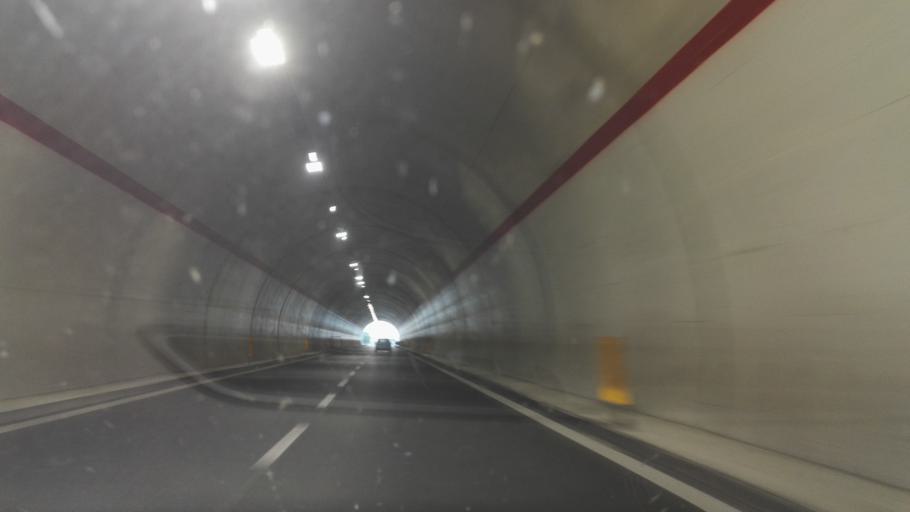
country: IT
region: Calabria
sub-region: Provincia di Reggio Calabria
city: Roccella Ionica
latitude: 38.3295
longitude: 16.4108
